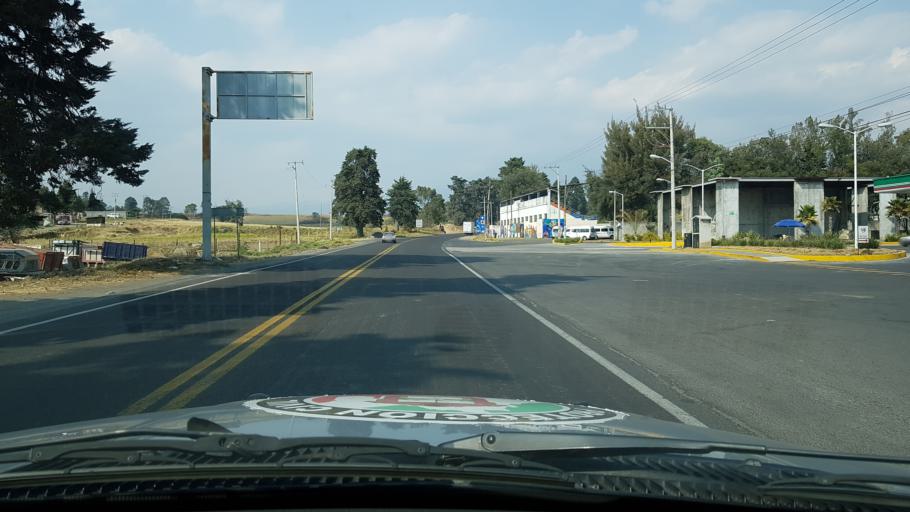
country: MX
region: Mexico
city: Ozumba de Alzate
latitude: 19.0371
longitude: -98.8079
